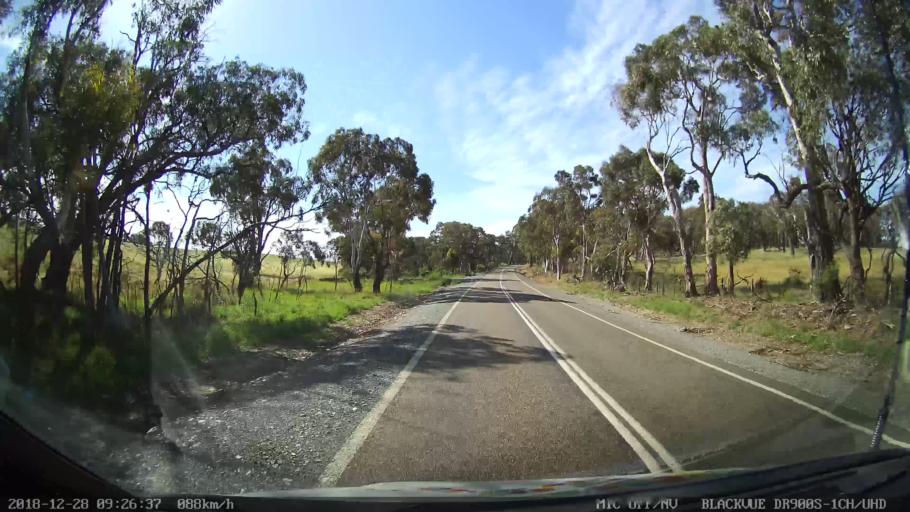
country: AU
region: New South Wales
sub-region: Upper Lachlan Shire
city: Crookwell
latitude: -34.4202
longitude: 149.4027
